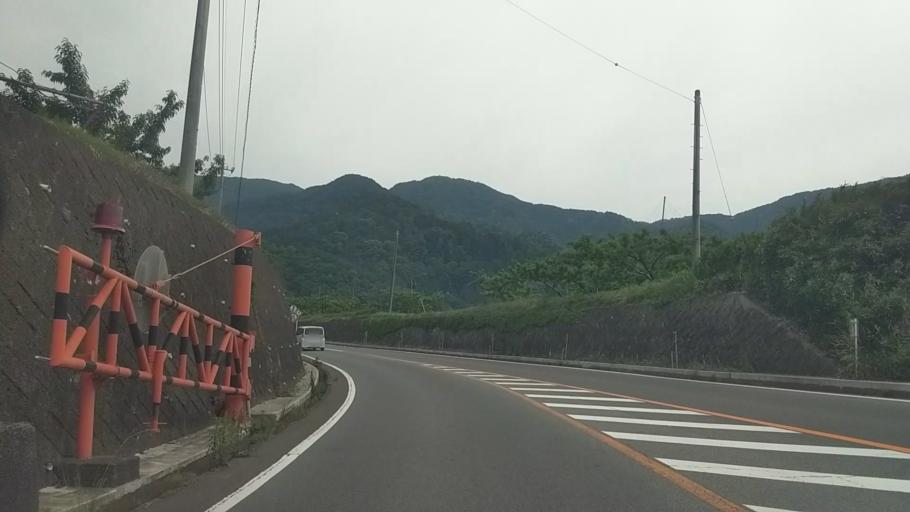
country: JP
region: Yamanashi
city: Isawa
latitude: 35.5731
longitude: 138.5905
